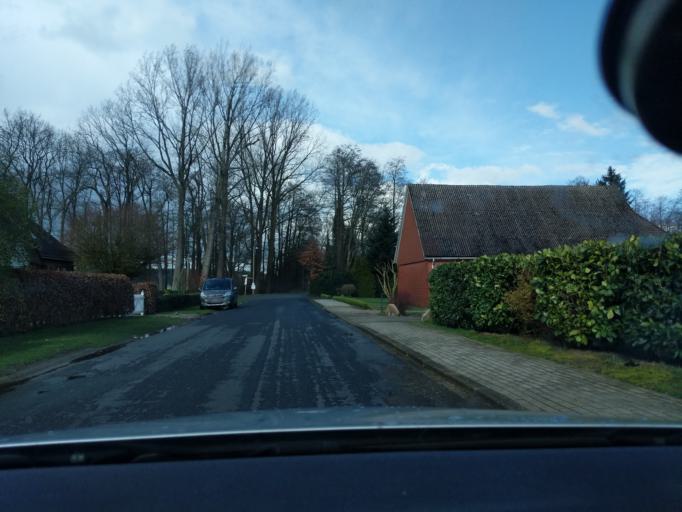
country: DE
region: Lower Saxony
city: Kranenburg
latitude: 53.6103
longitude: 9.2019
